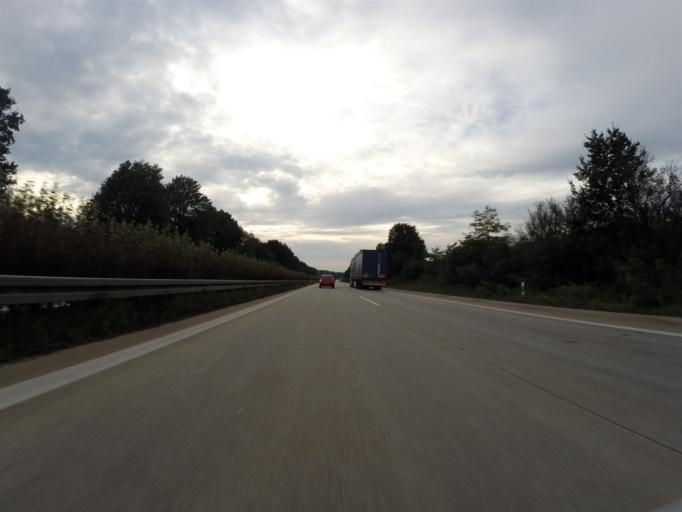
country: DE
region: Saxony
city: Nossen
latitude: 51.0816
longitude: 13.2900
